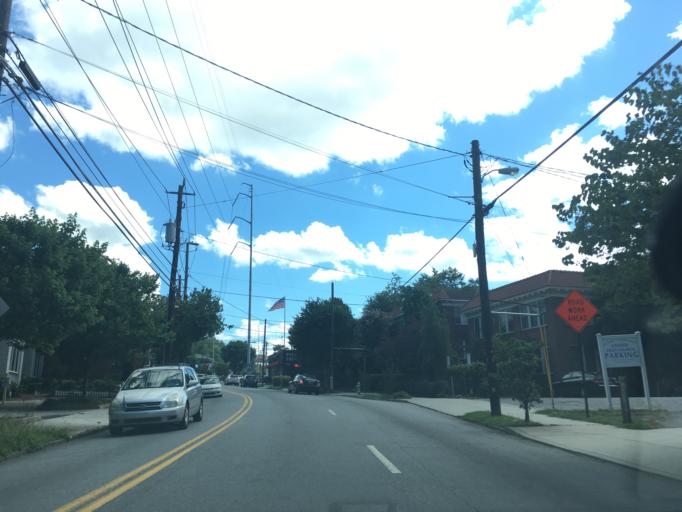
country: US
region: Georgia
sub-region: Fulton County
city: Atlanta
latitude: 33.7753
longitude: -84.3708
